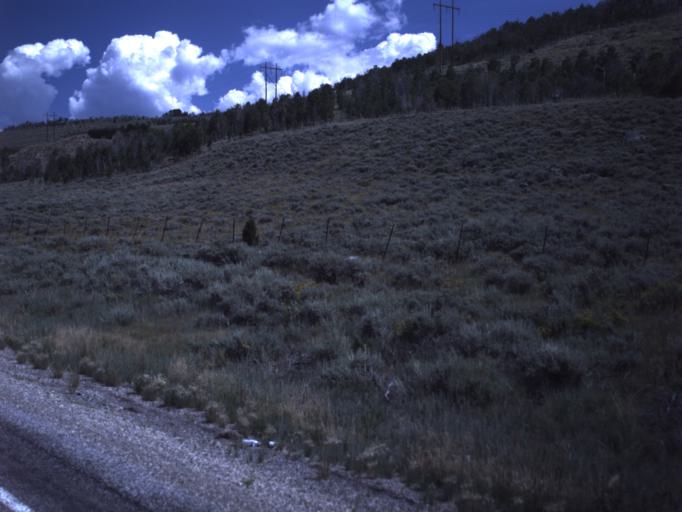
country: US
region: Utah
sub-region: Carbon County
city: Helper
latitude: 39.8166
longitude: -111.1353
